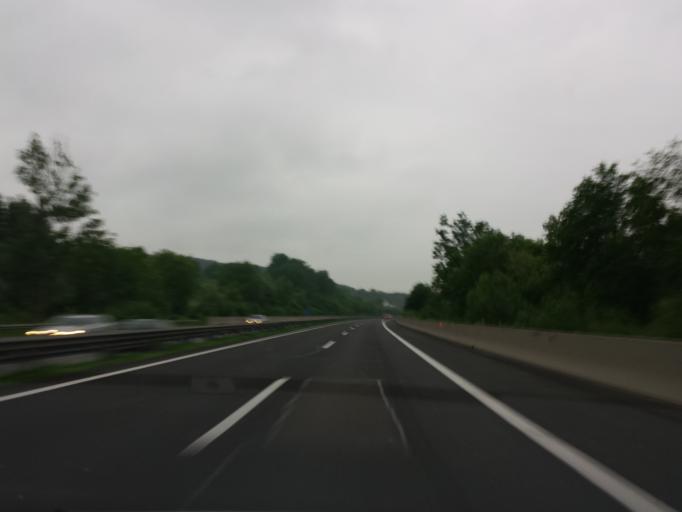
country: AT
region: Styria
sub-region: Politischer Bezirk Hartberg-Fuerstenfeld
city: Ilz
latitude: 47.0795
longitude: 15.8985
